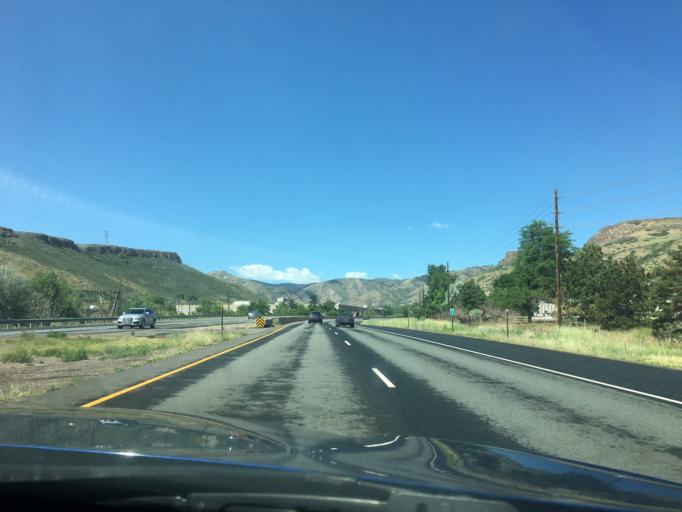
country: US
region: Colorado
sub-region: Jefferson County
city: Applewood
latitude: 39.7702
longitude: -105.1893
